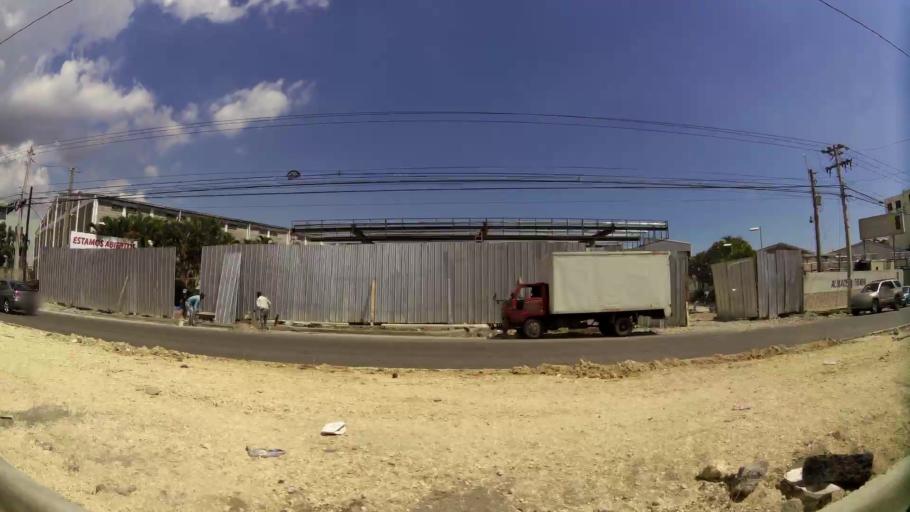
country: DO
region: Santo Domingo
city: Santo Domingo Oeste
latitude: 18.4889
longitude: -69.9998
